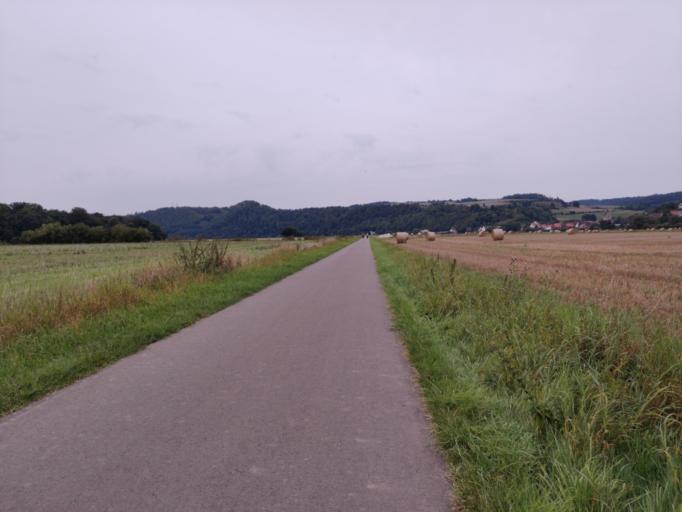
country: DE
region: Lower Saxony
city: Brevorde
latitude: 51.9063
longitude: 9.4370
